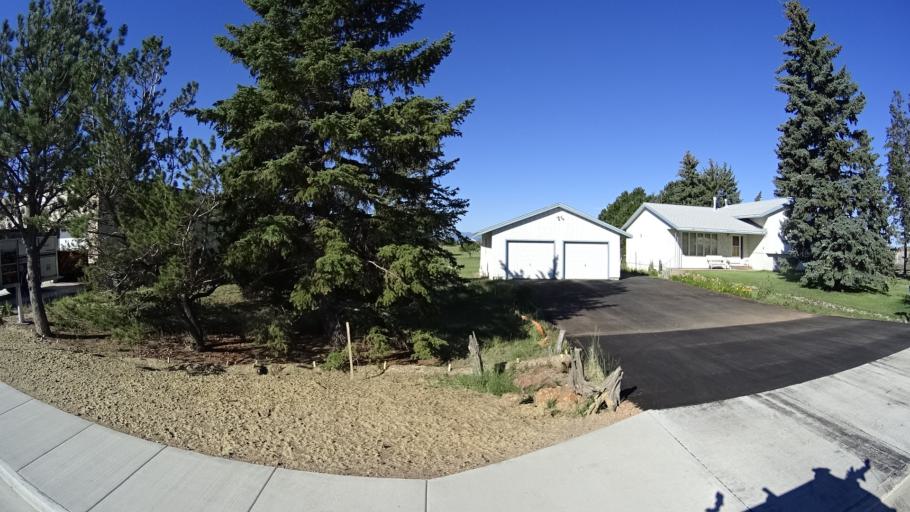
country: US
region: Colorado
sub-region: El Paso County
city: Cimarron Hills
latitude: 38.9342
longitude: -104.6096
